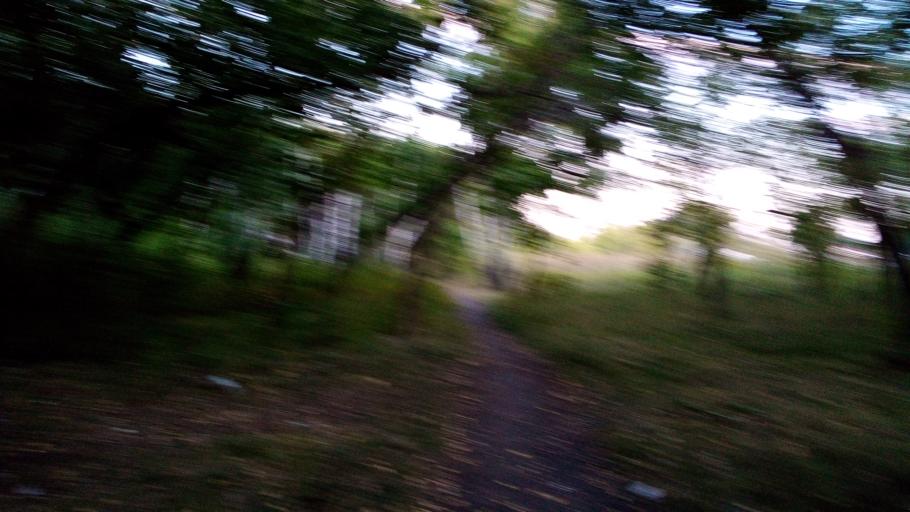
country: RU
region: Chelyabinsk
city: Potanino
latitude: 55.2879
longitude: 61.5111
